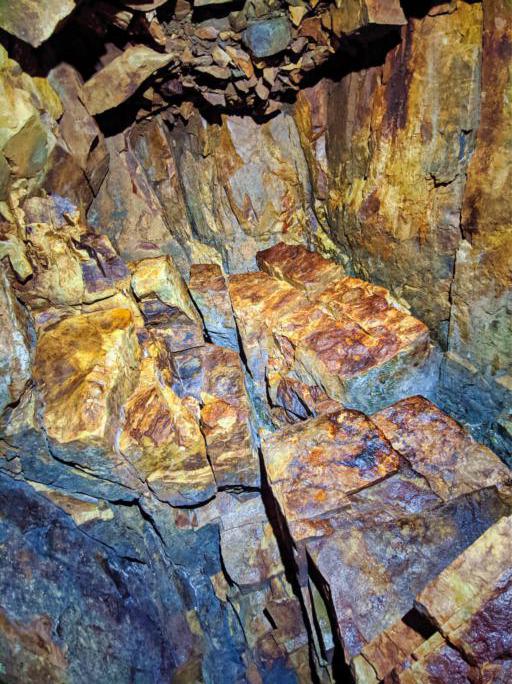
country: NO
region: Akershus
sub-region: Eidsvoll
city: Eidsvoll
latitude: 60.4232
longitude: 11.1943
